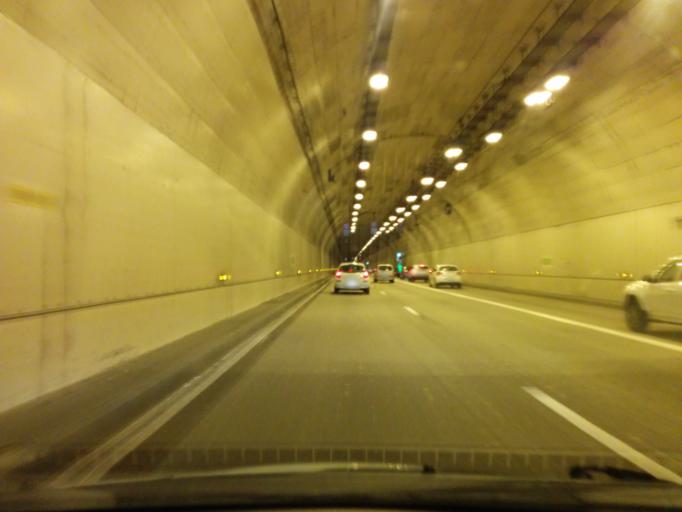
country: FR
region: Ile-de-France
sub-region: Departement des Hauts-de-Seine
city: Saint-Cloud
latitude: 48.8394
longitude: 2.2089
